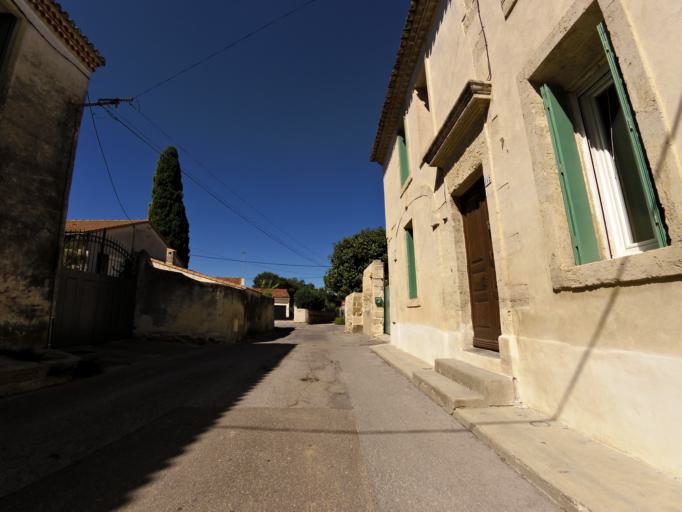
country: FR
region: Languedoc-Roussillon
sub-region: Departement du Gard
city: Codognan
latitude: 43.7332
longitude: 4.2175
